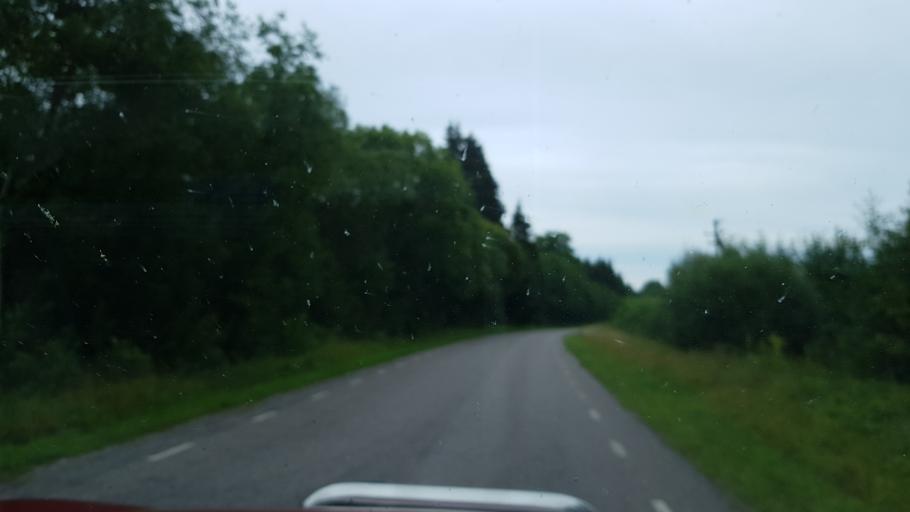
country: EE
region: Laeaene
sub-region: Lihula vald
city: Lihula
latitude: 58.8769
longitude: 23.8101
